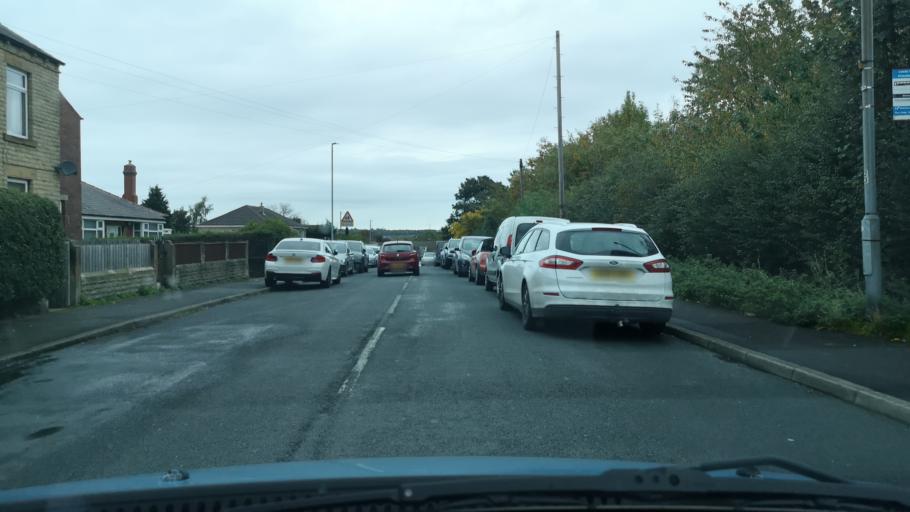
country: GB
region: England
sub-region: Kirklees
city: Heckmondwike
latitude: 53.7195
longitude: -1.6692
